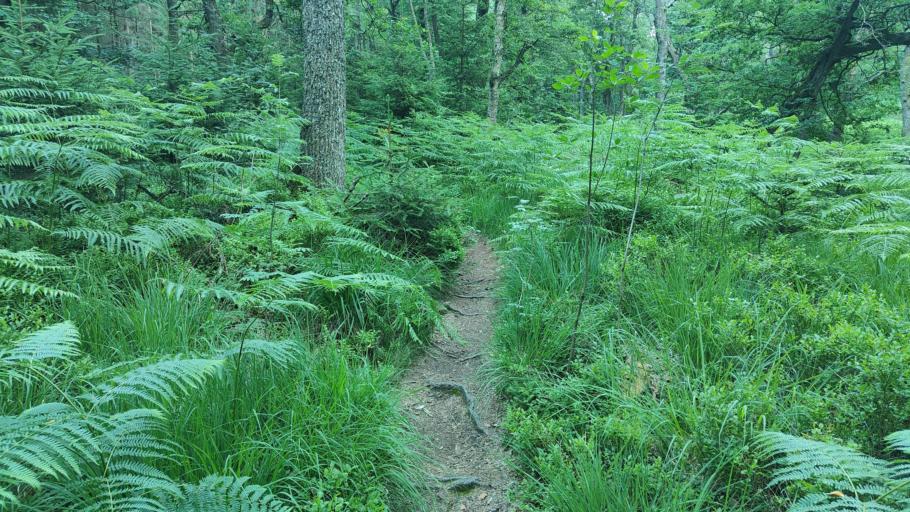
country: DE
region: North Rhine-Westphalia
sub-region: Regierungsbezirk Koln
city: Roetgen
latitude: 50.6220
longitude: 6.1545
